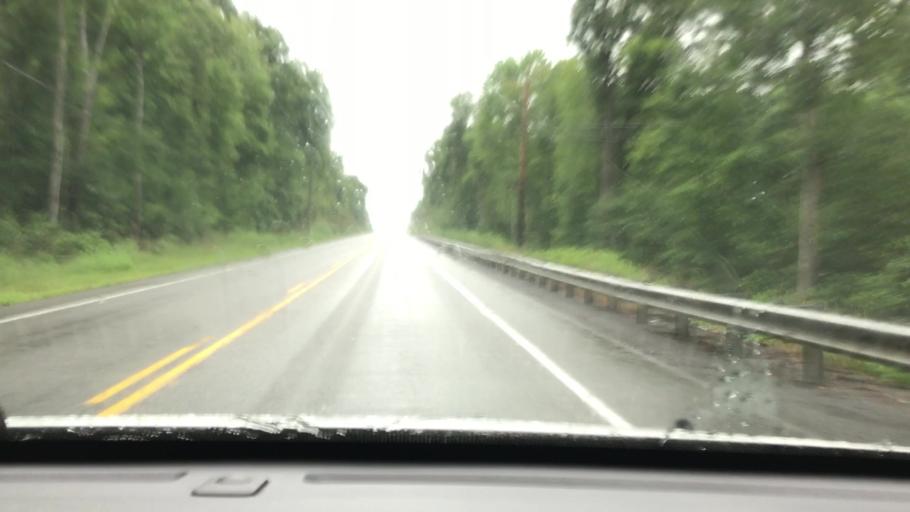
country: US
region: Pennsylvania
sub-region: Clearfield County
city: Osceola Mills
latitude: 40.8357
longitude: -78.2236
